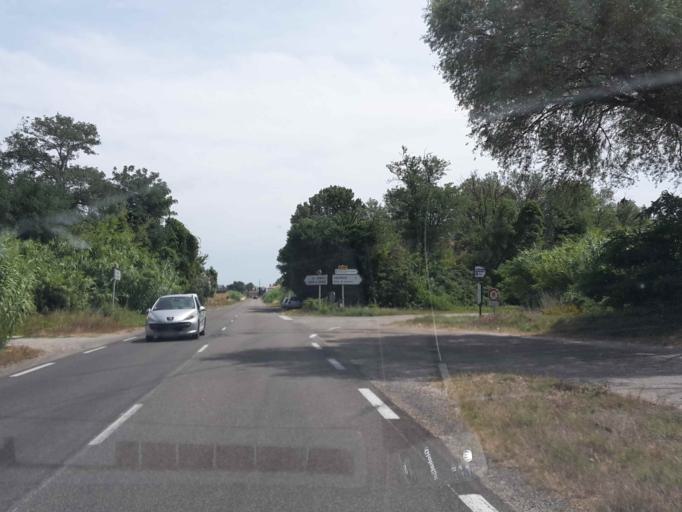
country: FR
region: Provence-Alpes-Cote d'Azur
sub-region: Departement des Bouches-du-Rhone
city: Arles
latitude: 43.6350
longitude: 4.6063
